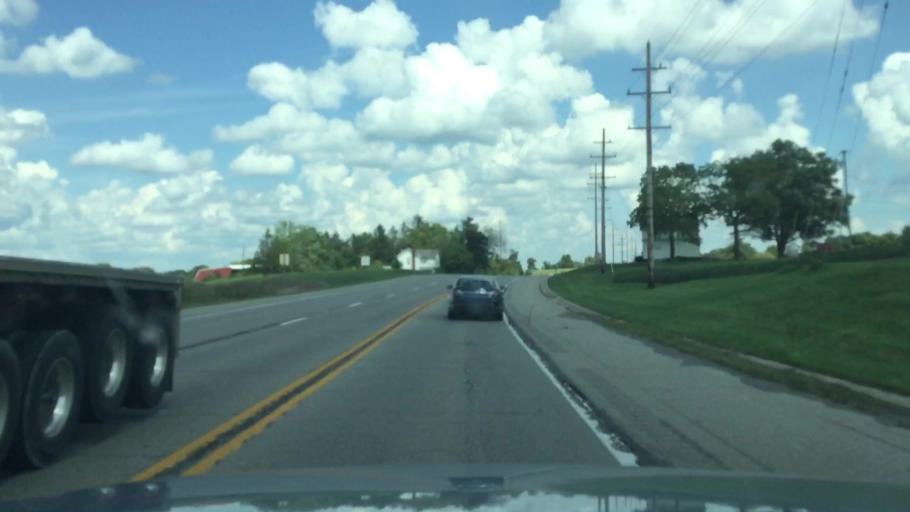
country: US
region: Michigan
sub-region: Washtenaw County
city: Saline
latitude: 42.1378
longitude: -83.8496
